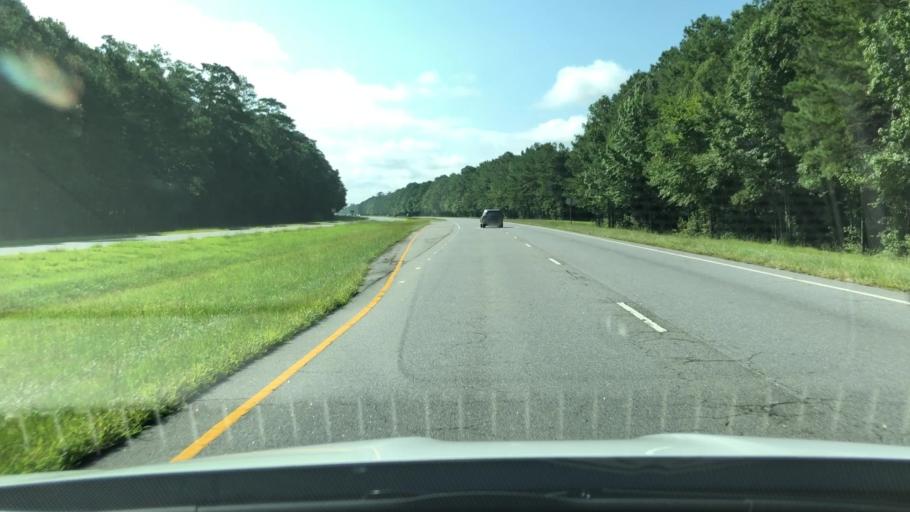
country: US
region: North Carolina
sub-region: Pasquotank County
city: Elizabeth City
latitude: 36.4065
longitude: -76.3378
